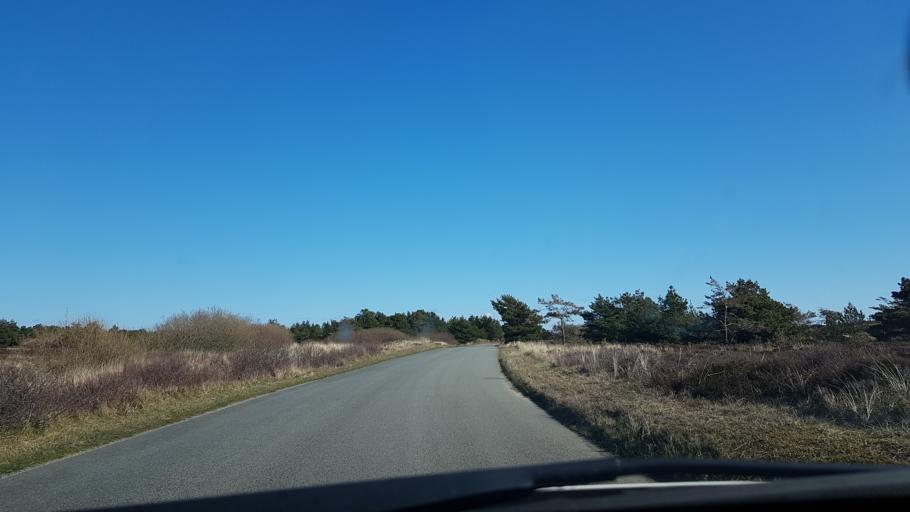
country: DE
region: Schleswig-Holstein
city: List
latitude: 55.1601
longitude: 8.5324
